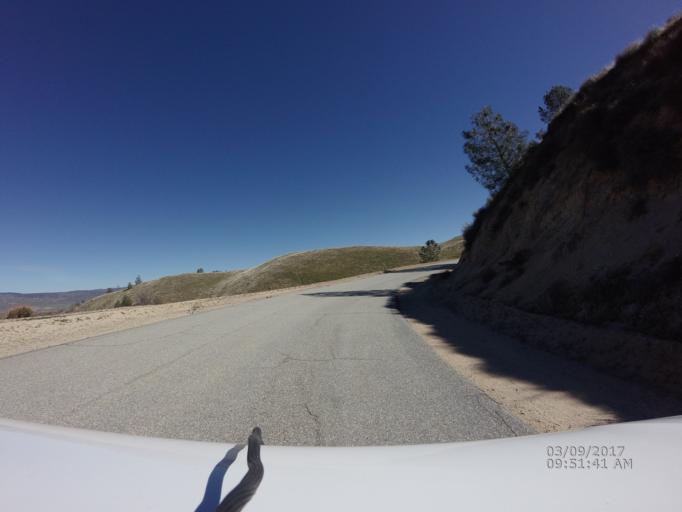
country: US
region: California
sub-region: Kern County
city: Lebec
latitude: 34.7479
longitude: -118.7027
